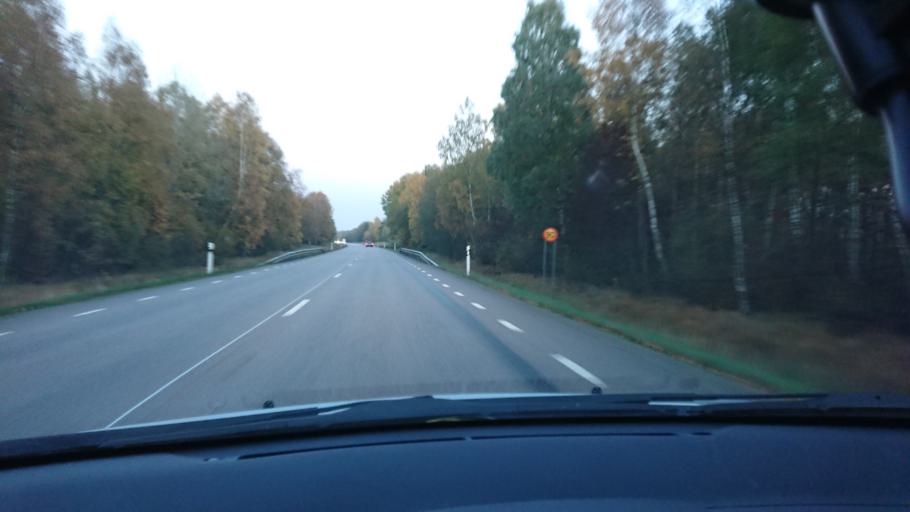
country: SE
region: Kronoberg
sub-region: Markaryds Kommun
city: Stromsnasbruk
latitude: 56.7554
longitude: 13.7259
